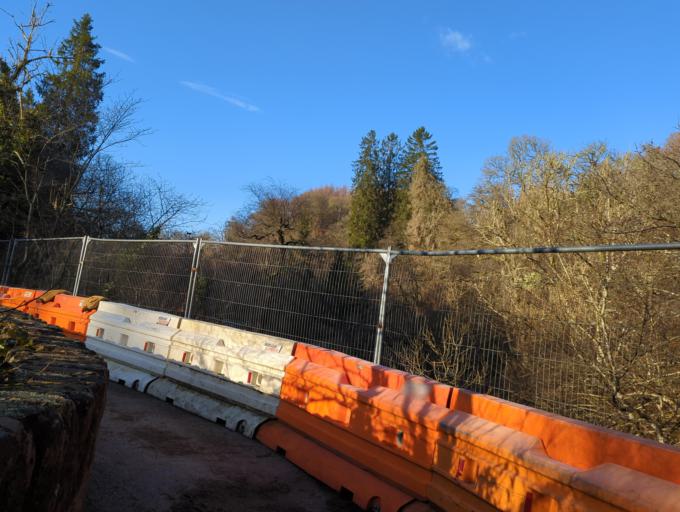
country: GB
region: Scotland
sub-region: Perth and Kinross
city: Bankfoot
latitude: 56.5523
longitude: -3.6337
